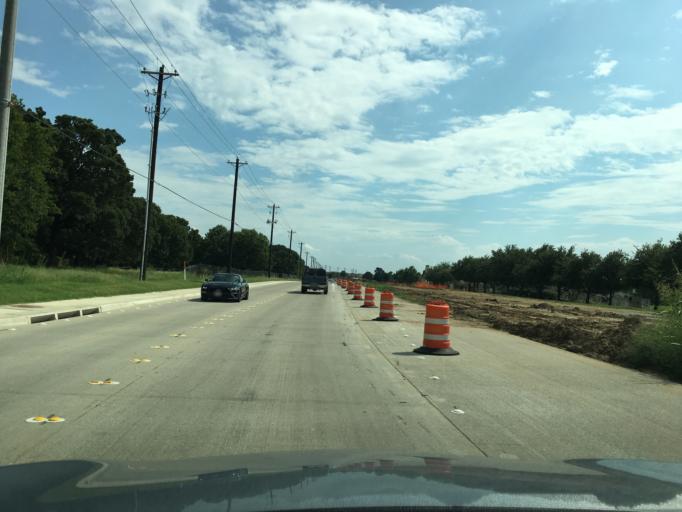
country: US
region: Texas
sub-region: Denton County
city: Oak Point
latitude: 33.2092
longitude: -96.9749
